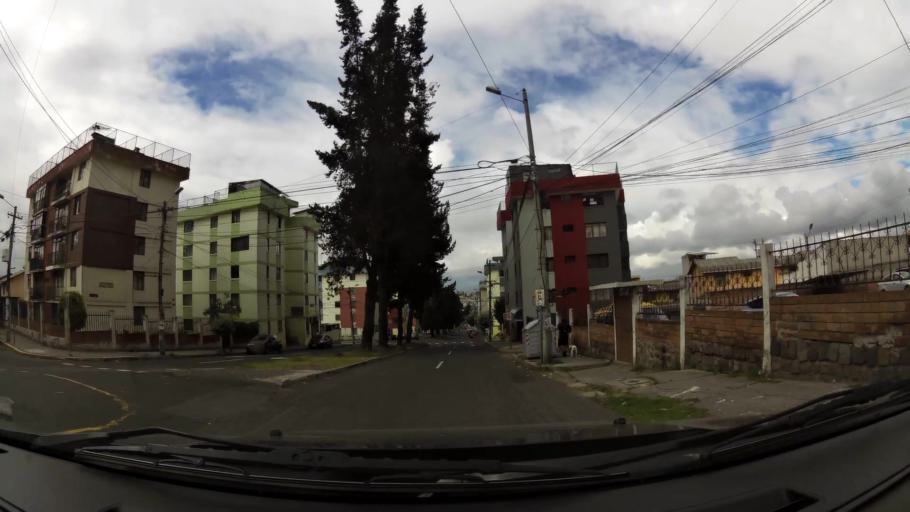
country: EC
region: Pichincha
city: Quito
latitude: -0.1375
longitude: -78.5009
